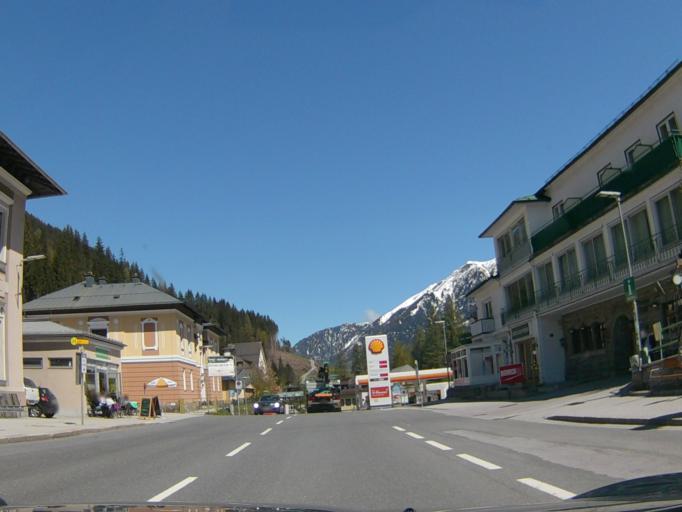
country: AT
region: Salzburg
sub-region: Politischer Bezirk Sankt Johann im Pongau
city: Bad Gastein
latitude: 47.1121
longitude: 13.1325
